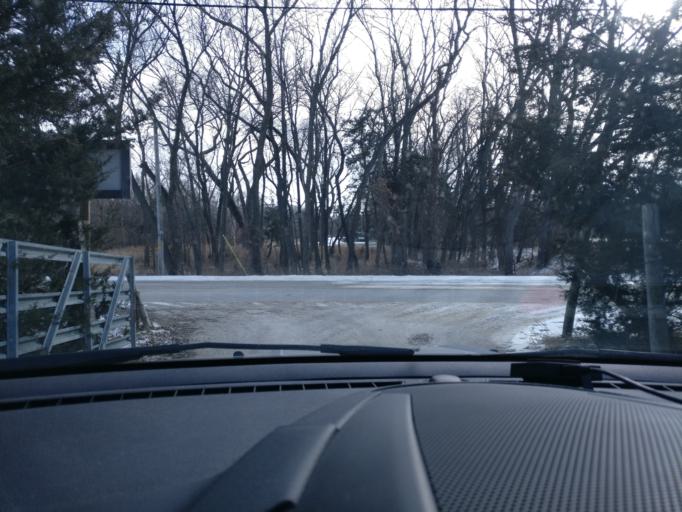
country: US
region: Nebraska
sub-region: Dodge County
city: Fremont
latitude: 41.4189
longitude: -96.5222
